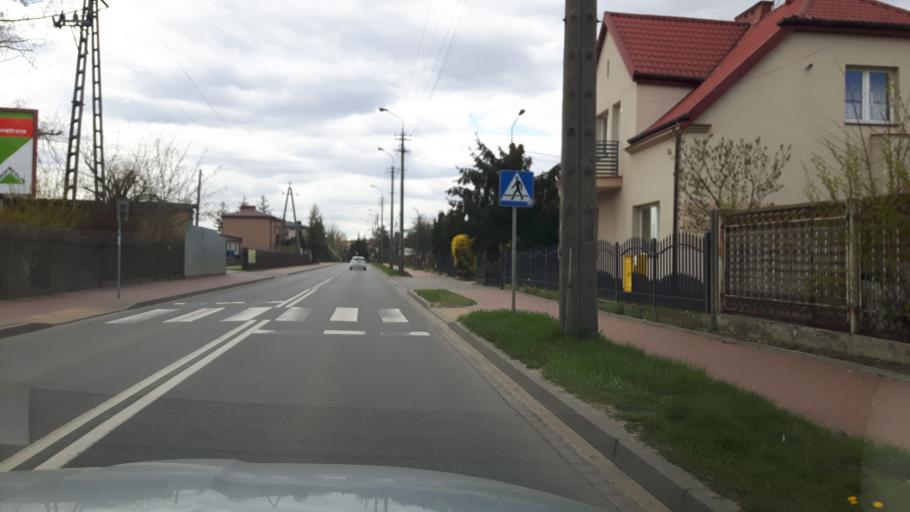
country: PL
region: Masovian Voivodeship
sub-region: Powiat wolominski
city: Wolomin
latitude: 52.3532
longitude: 21.2518
